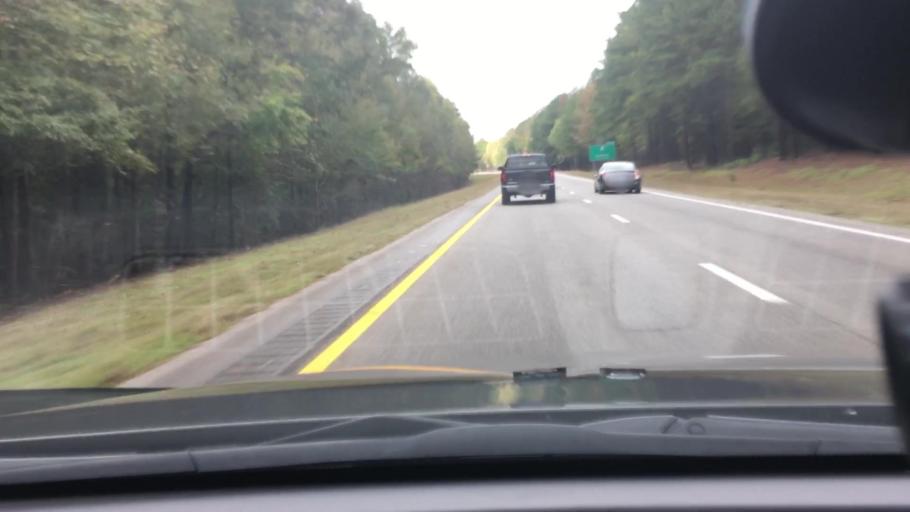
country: US
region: North Carolina
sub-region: Wake County
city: Zebulon
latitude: 35.7964
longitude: -78.1672
